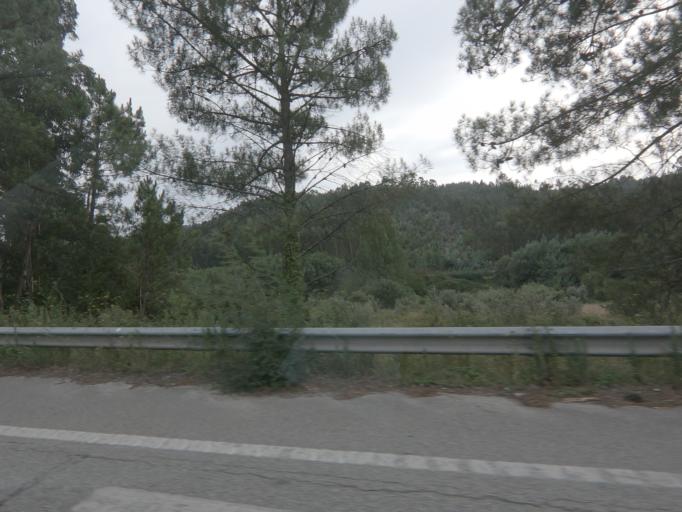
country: PT
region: Coimbra
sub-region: Penacova
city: Lorvao
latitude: 40.3015
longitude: -8.3162
